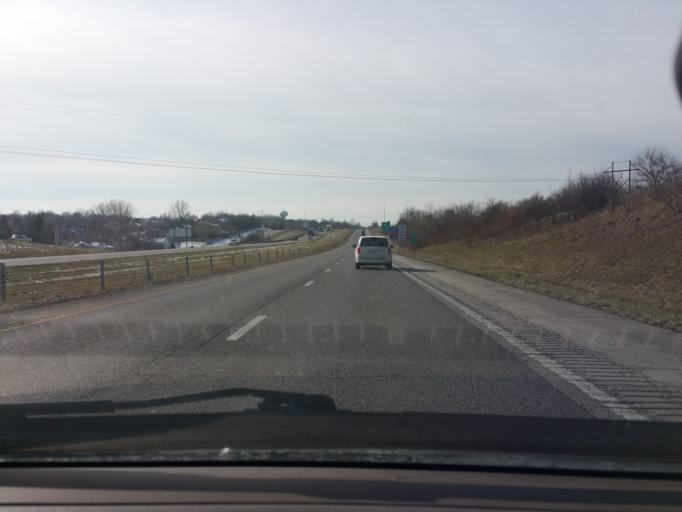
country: US
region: Missouri
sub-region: Clay County
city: Liberty
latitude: 39.2736
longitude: -94.4306
